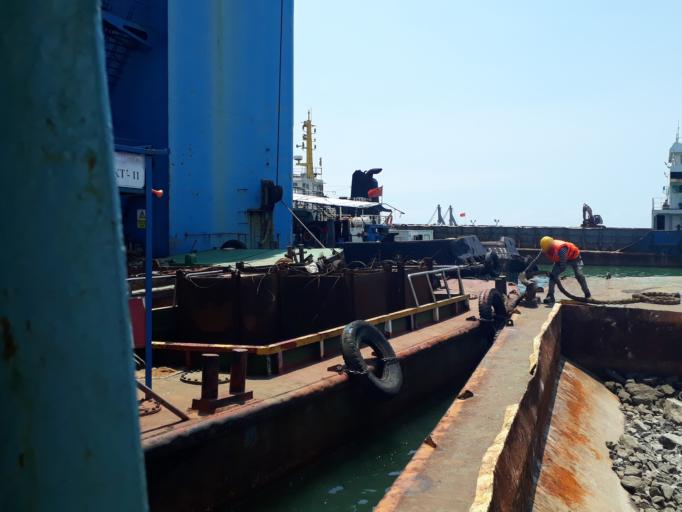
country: LK
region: Western
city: Colombo
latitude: 6.9251
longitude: 79.8366
